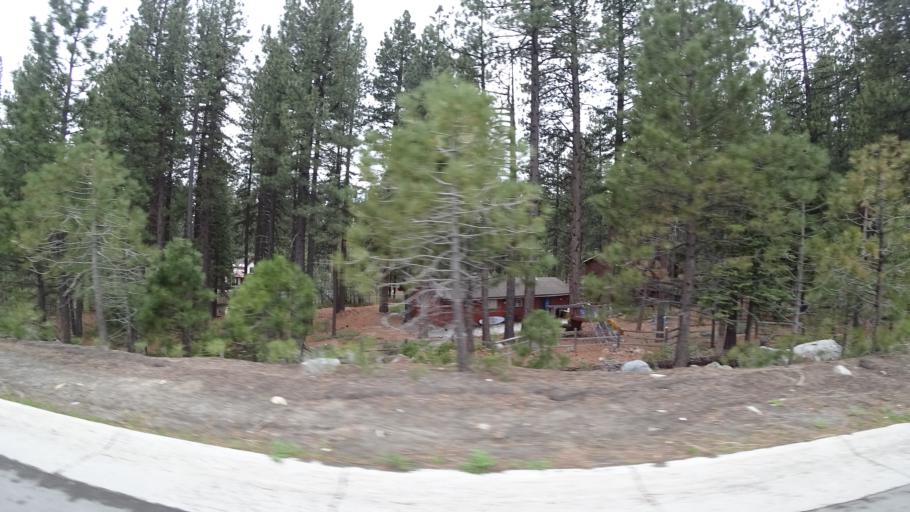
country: US
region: Nevada
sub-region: Washoe County
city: Incline Village
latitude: 39.2409
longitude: -119.9308
